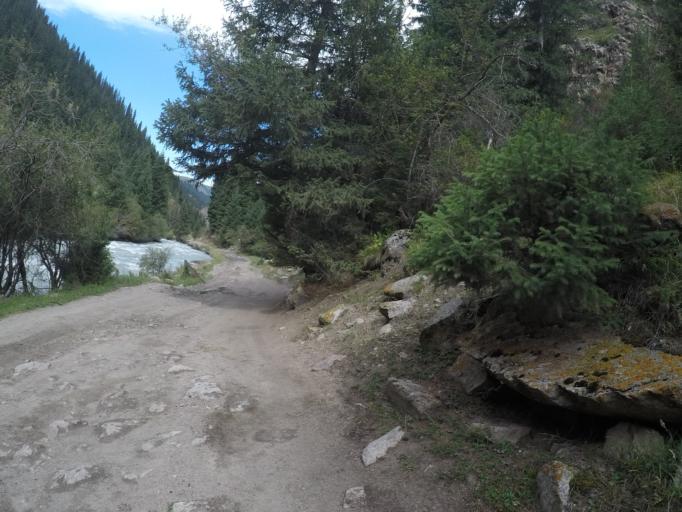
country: KG
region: Ysyk-Koel
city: Teploklyuchenka
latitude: 42.4432
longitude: 78.5515
